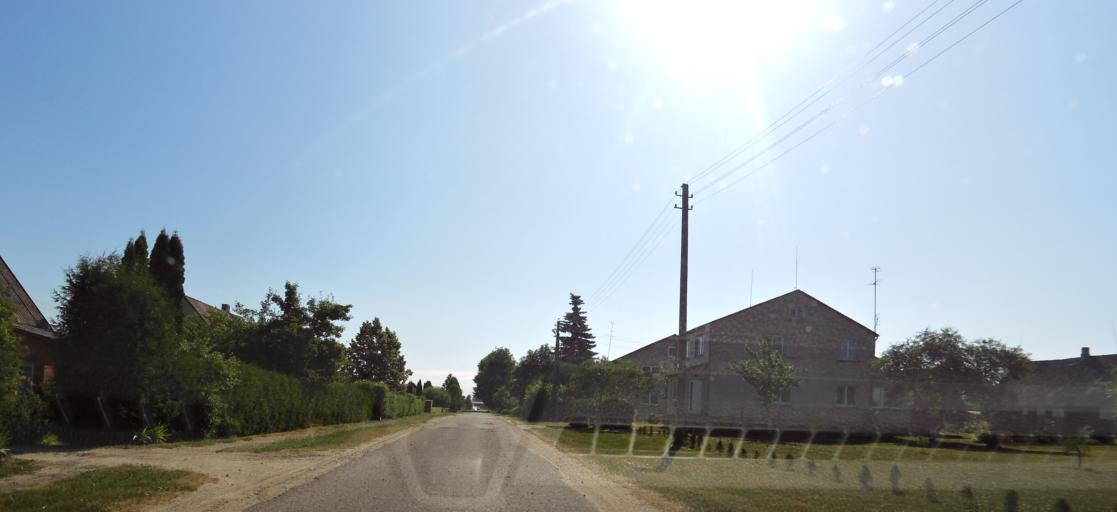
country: LT
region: Panevezys
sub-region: Birzai
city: Birzai
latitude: 56.2451
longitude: 24.8601
